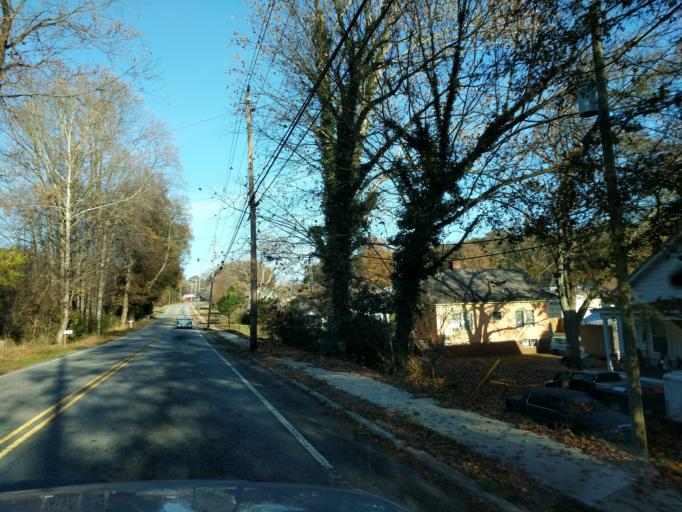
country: US
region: South Carolina
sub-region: Spartanburg County
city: Arcadia
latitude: 34.9577
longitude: -81.9917
